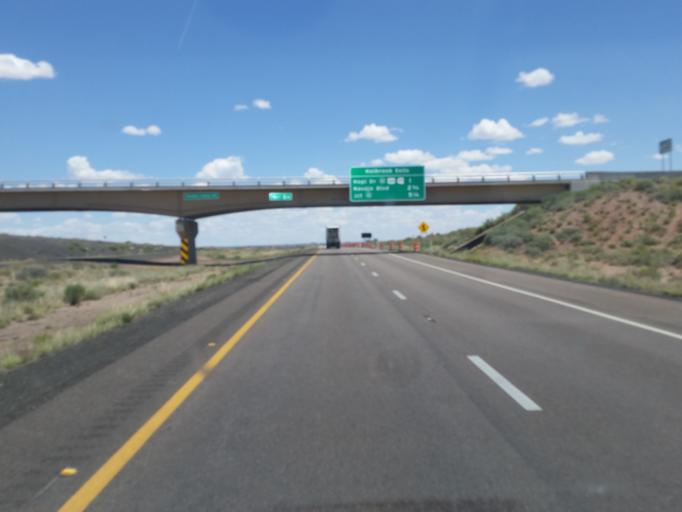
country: US
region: Arizona
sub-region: Navajo County
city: Holbrook
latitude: 34.9073
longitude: -110.2132
